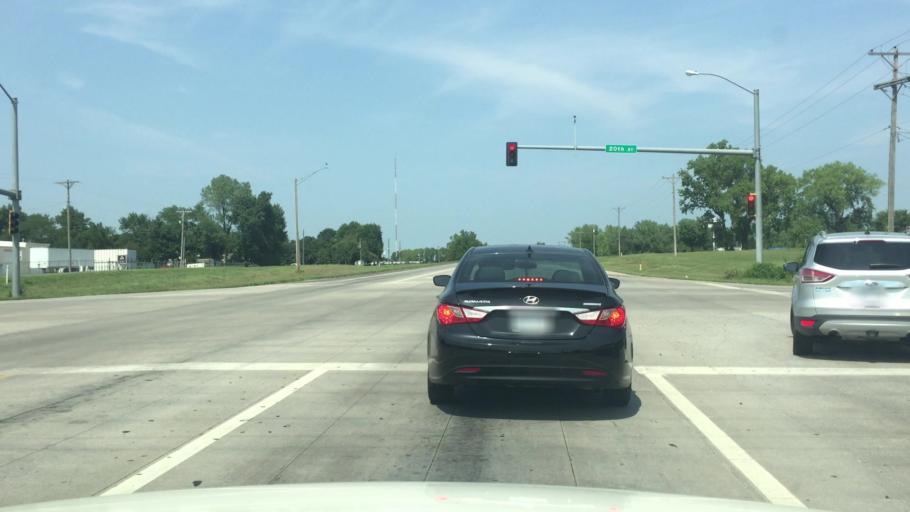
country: US
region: Kansas
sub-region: Crawford County
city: Pittsburg
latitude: 37.4255
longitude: -94.7162
